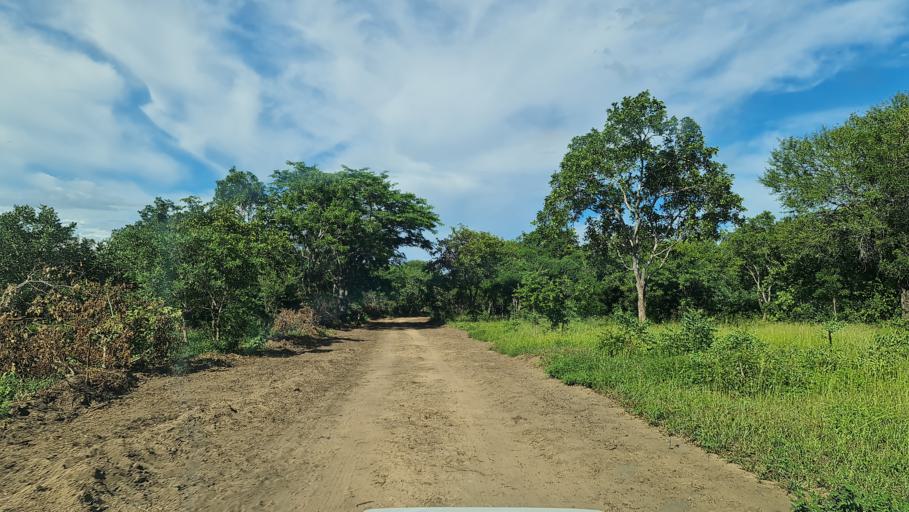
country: MZ
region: Nampula
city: Antonio Enes
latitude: -15.5107
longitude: 40.1337
